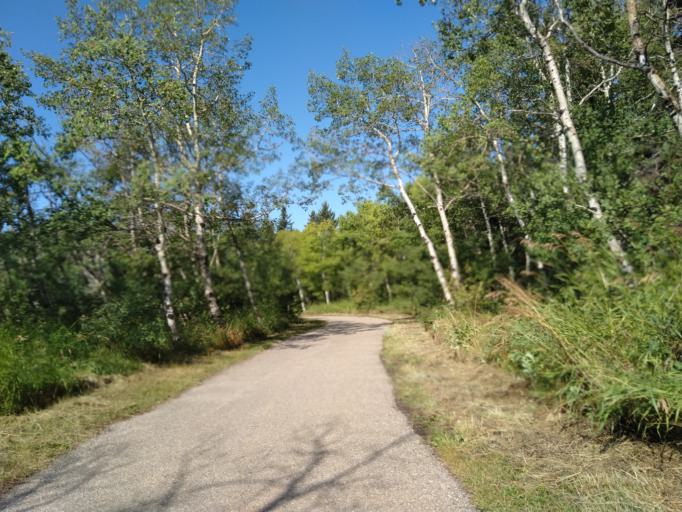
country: CA
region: Alberta
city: Calgary
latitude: 51.0962
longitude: -114.2425
